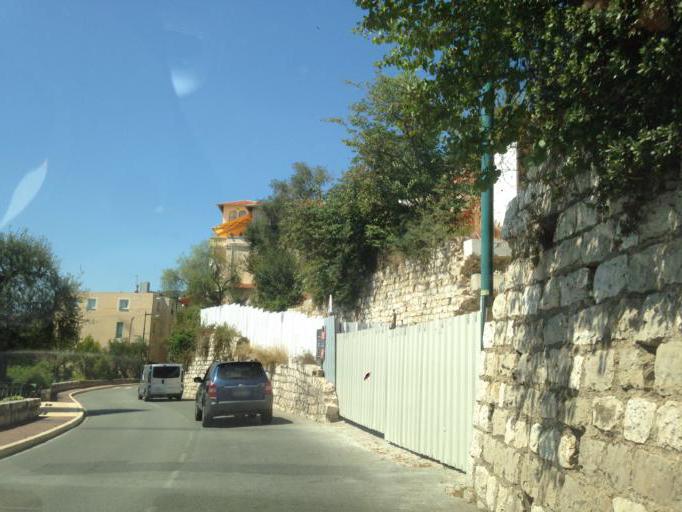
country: FR
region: Provence-Alpes-Cote d'Azur
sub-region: Departement des Alpes-Maritimes
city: Saint-Jean-Cap-Ferrat
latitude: 43.6970
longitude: 7.3272
